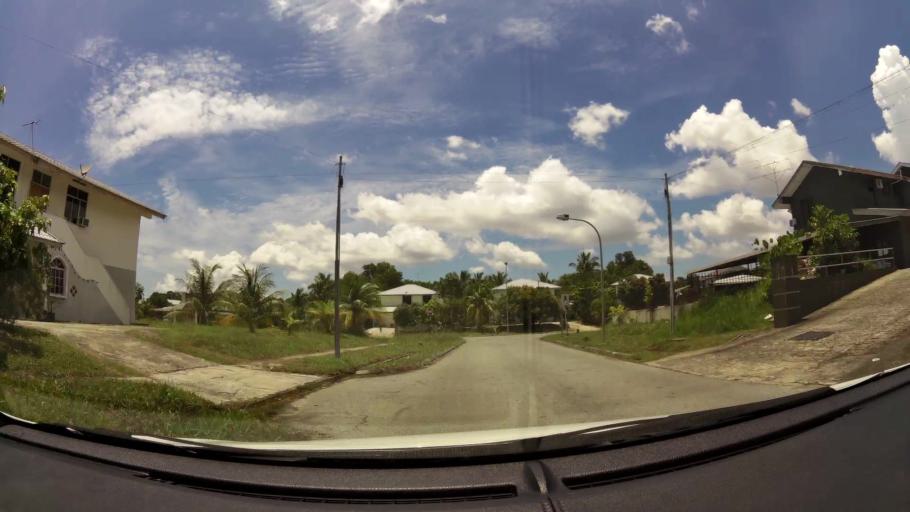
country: BN
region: Brunei and Muara
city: Bandar Seri Begawan
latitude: 4.9632
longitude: 114.9227
